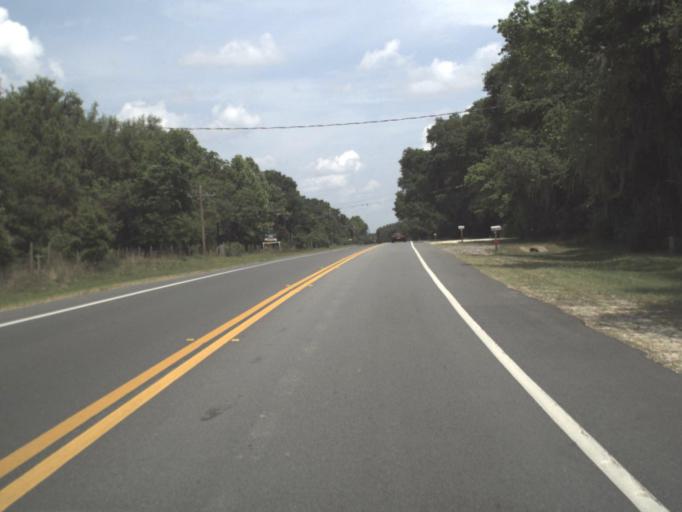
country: US
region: Florida
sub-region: Alachua County
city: Hawthorne
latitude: 29.6099
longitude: -82.0053
